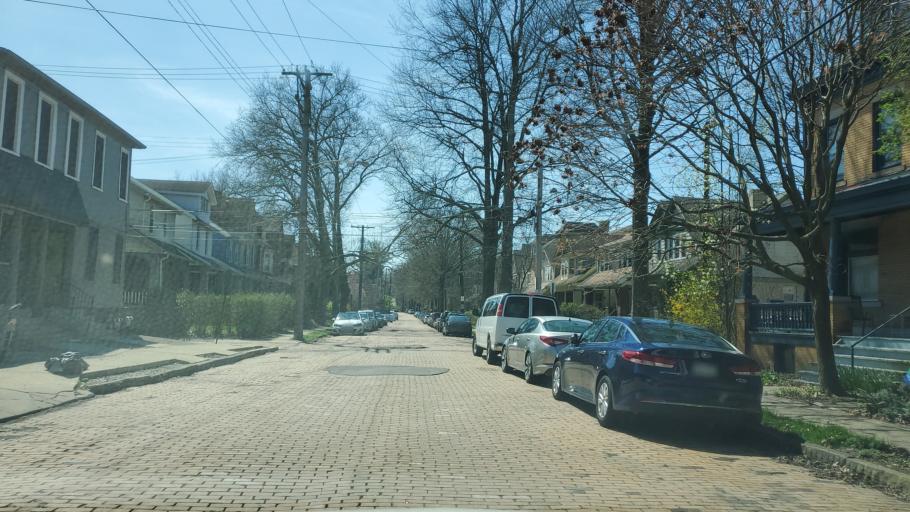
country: US
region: Pennsylvania
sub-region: Allegheny County
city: Wilkinsburg
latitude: 40.4408
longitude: -79.8934
